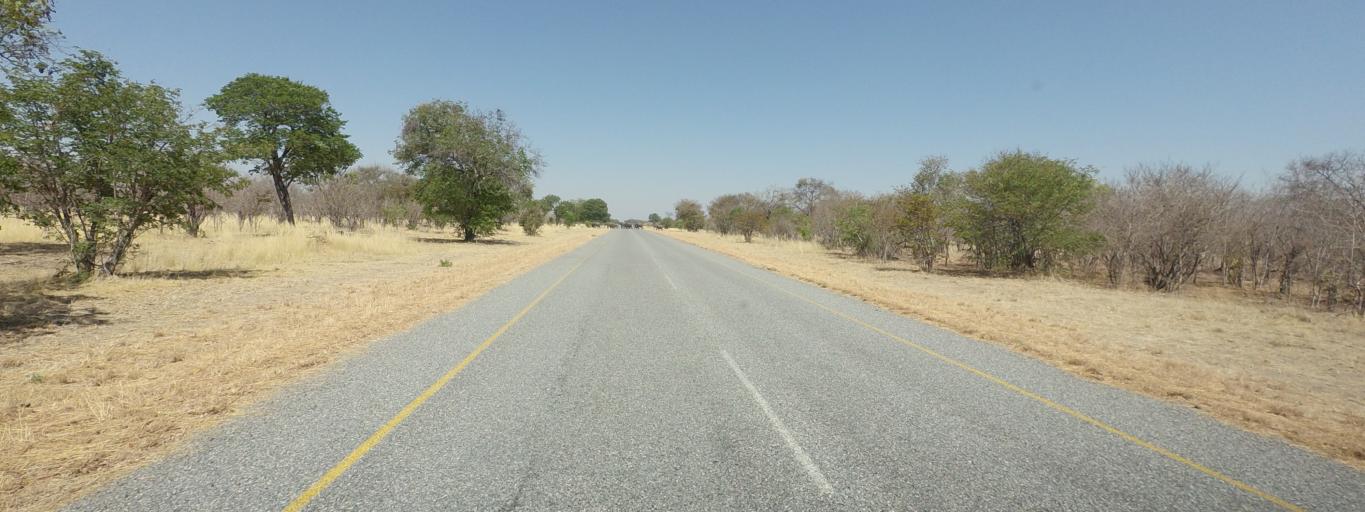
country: BW
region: North West
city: Kasane
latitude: -17.9219
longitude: 24.9410
